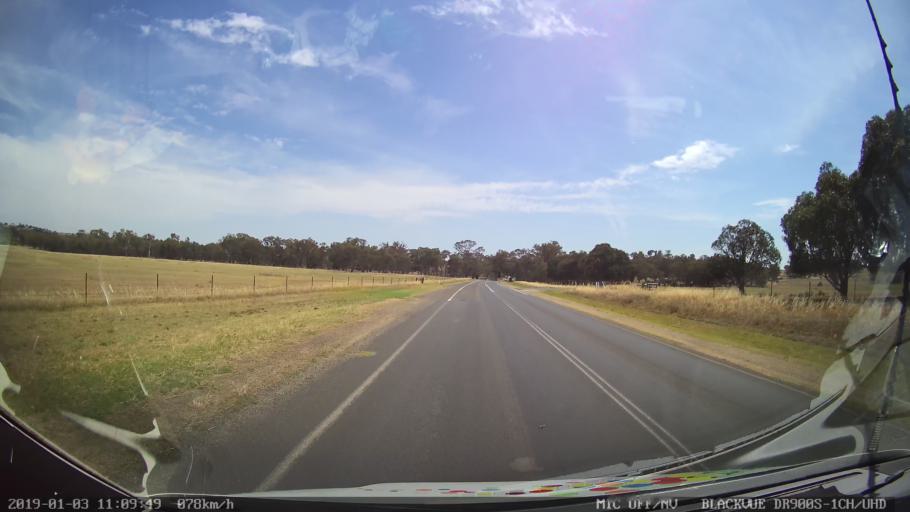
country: AU
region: New South Wales
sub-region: Young
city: Young
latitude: -34.2338
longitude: 148.2561
